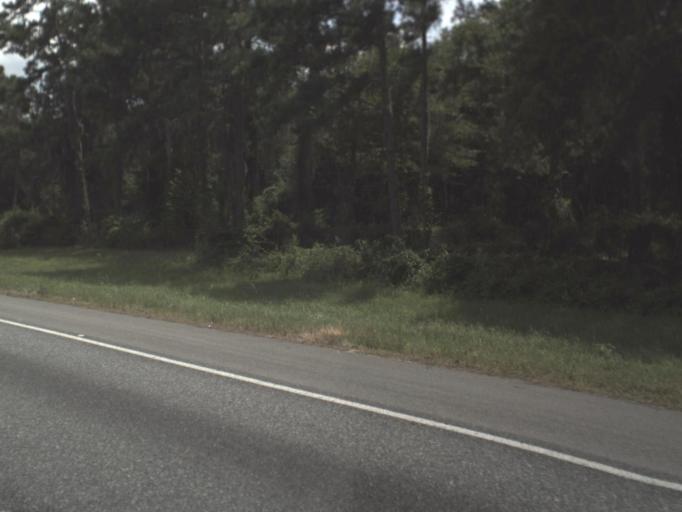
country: US
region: Florida
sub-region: Suwannee County
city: Live Oak
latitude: 30.3861
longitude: -82.8733
